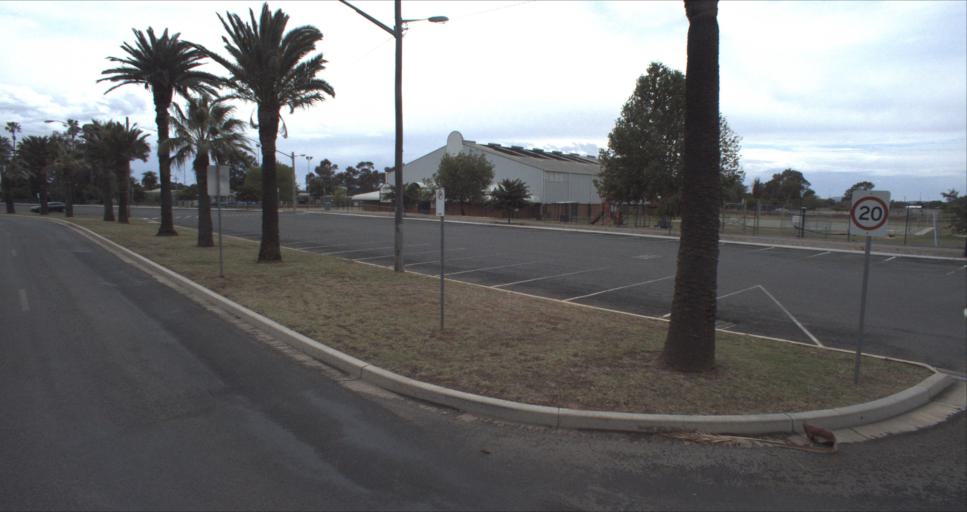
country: AU
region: New South Wales
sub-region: Leeton
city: Leeton
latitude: -34.5517
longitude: 146.4116
